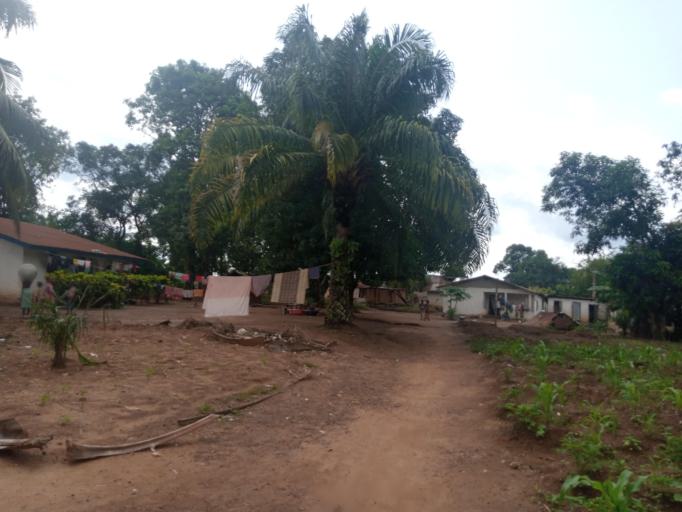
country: SL
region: Southern Province
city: Baoma
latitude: 7.9841
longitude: -11.7302
